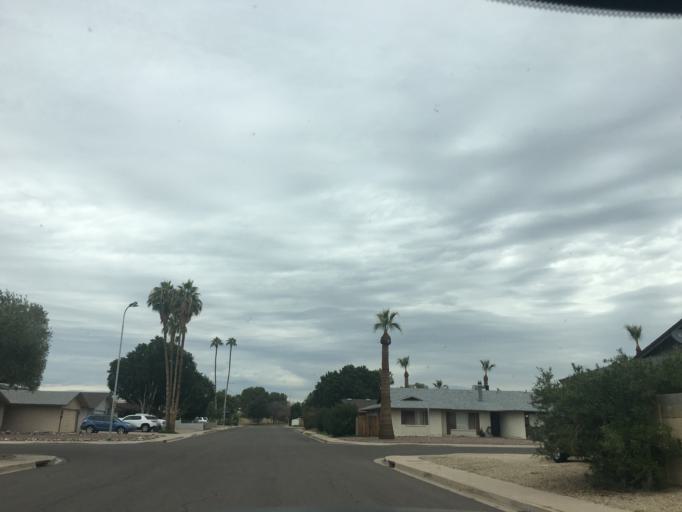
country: US
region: Arizona
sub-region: Maricopa County
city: Tempe
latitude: 33.3816
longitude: -111.9174
